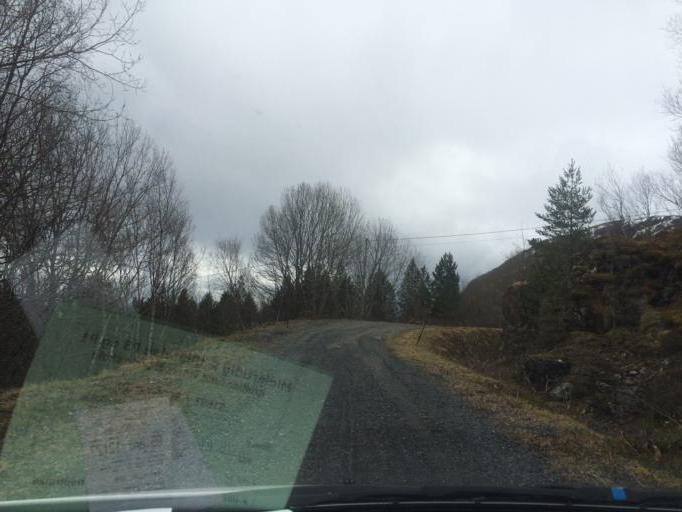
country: NO
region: More og Romsdal
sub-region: Gjemnes
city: Batnfjordsora
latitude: 62.9654
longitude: 7.7318
